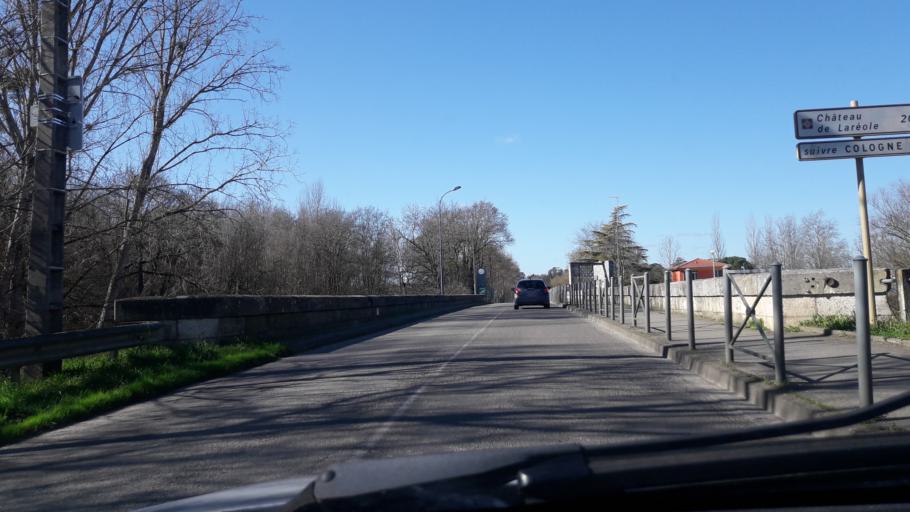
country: FR
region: Midi-Pyrenees
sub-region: Departement du Gers
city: Pujaudran
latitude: 43.6142
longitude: 1.0761
